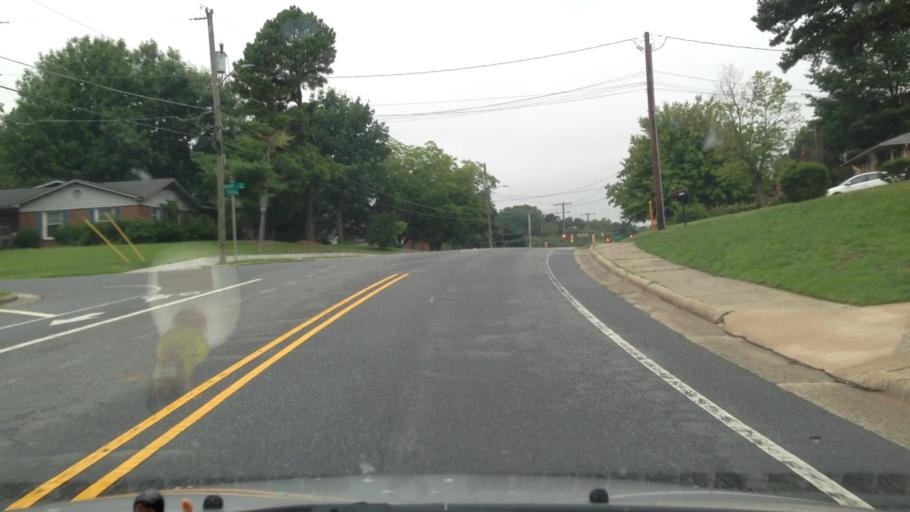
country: US
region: North Carolina
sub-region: Guilford County
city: Greensboro
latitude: 36.0544
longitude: -79.7713
